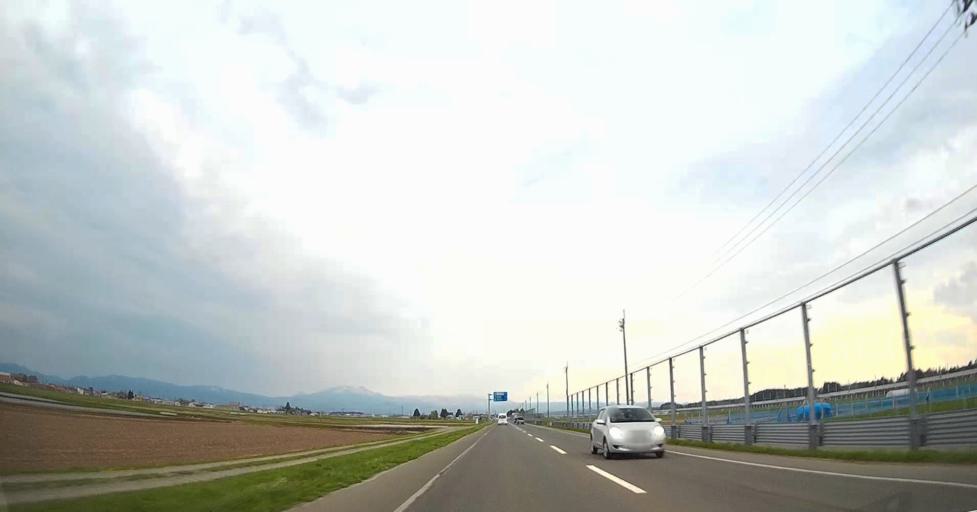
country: JP
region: Aomori
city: Aomori Shi
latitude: 40.8747
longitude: 140.6731
